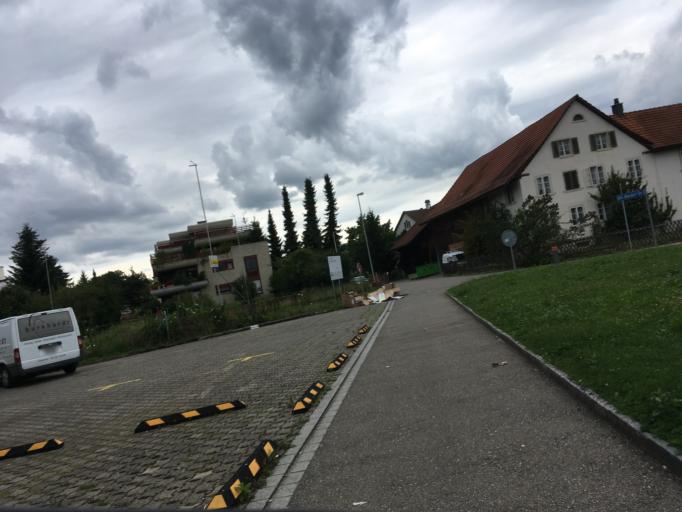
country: CH
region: Zurich
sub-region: Bezirk Uster
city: Dubendorf
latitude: 47.3937
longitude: 8.6228
